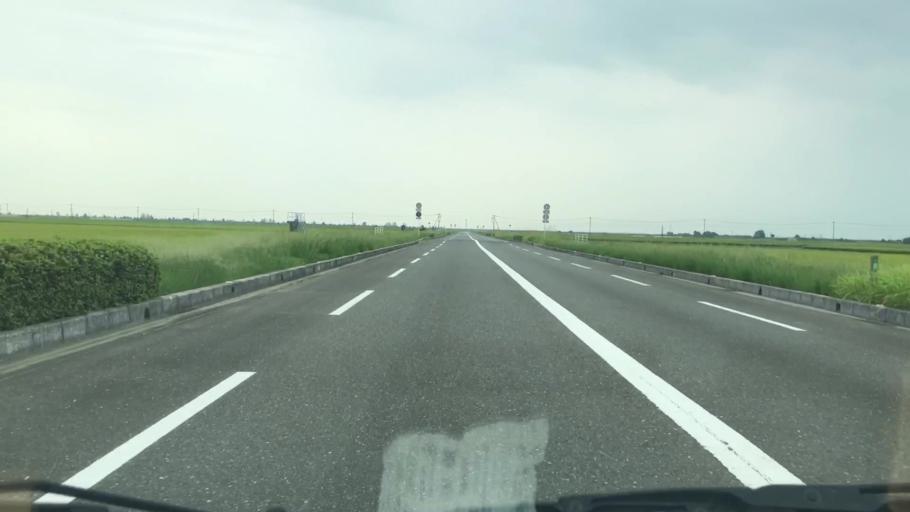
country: JP
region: Saga Prefecture
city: Okawa
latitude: 33.1758
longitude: 130.2969
